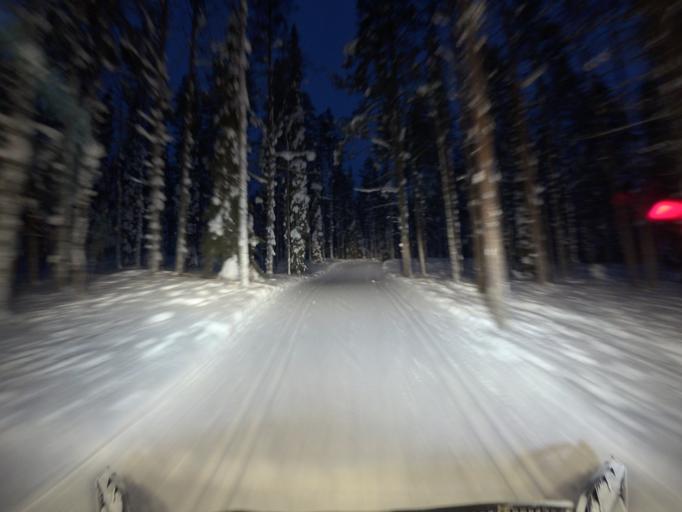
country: FI
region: Lapland
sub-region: Tunturi-Lappi
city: Kolari
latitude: 67.6018
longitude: 24.1246
